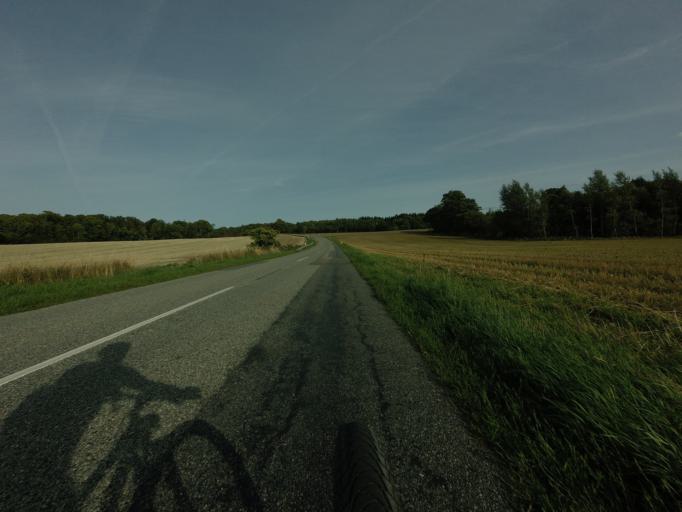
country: DK
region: Zealand
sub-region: Faxe Kommune
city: Fakse
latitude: 55.1985
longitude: 12.1133
